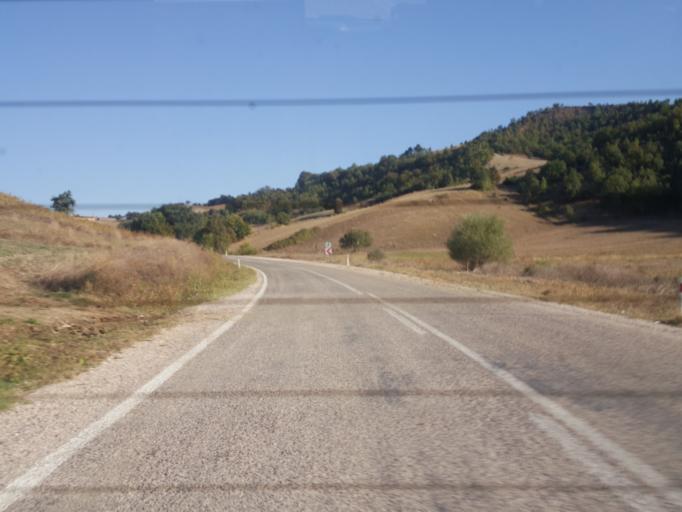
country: TR
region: Amasya
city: Tasova
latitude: 40.7192
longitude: 36.3050
